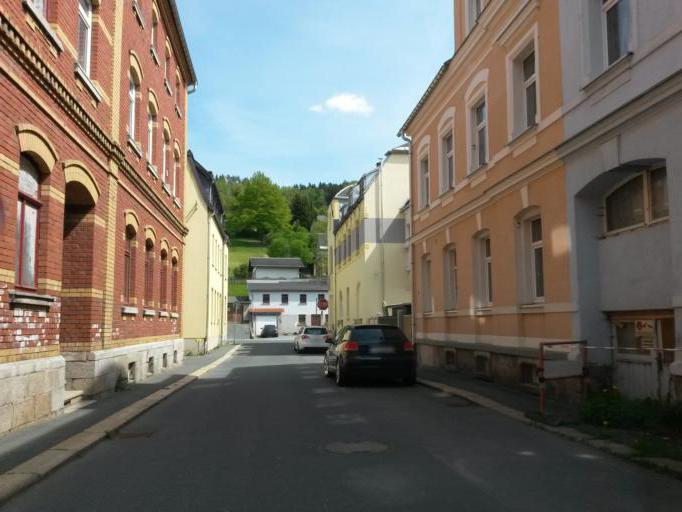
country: DE
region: Saxony
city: Klingenthal
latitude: 50.3689
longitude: 12.4687
